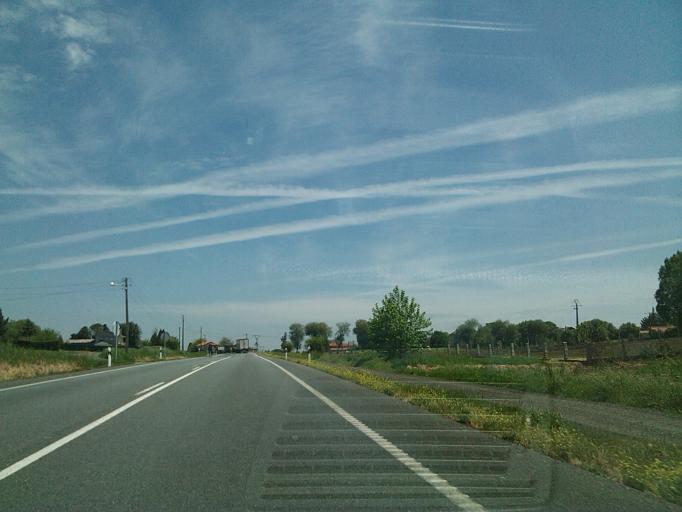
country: ES
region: Galicia
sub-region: Provincia da Coruna
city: Frades
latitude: 43.0337
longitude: -8.2282
